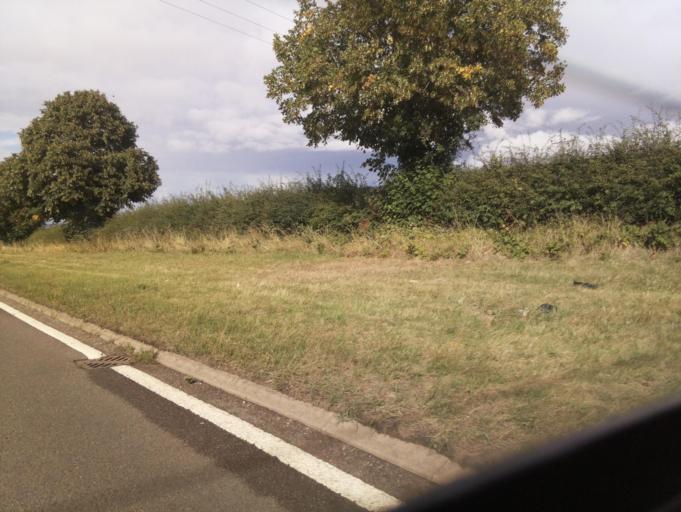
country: GB
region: England
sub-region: Shropshire
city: Ryton
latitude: 52.5899
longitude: -2.3983
